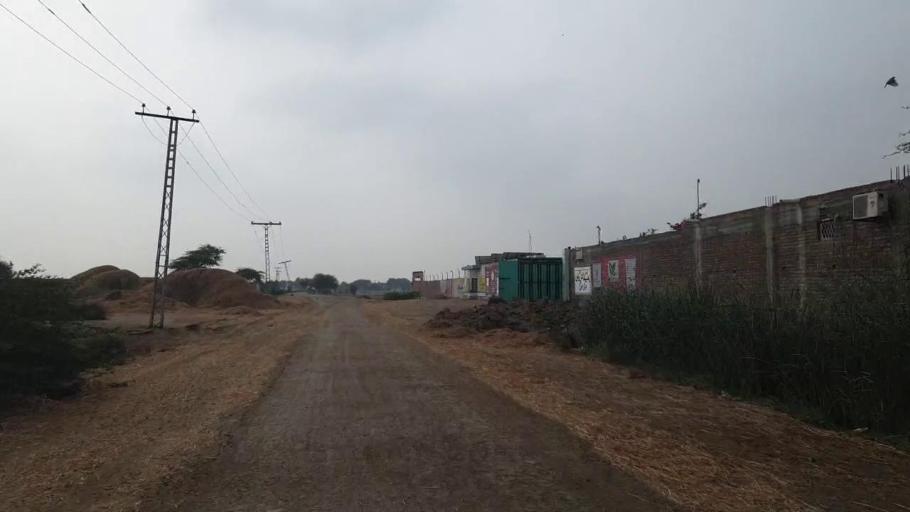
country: PK
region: Sindh
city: Matli
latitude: 24.9392
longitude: 68.5752
